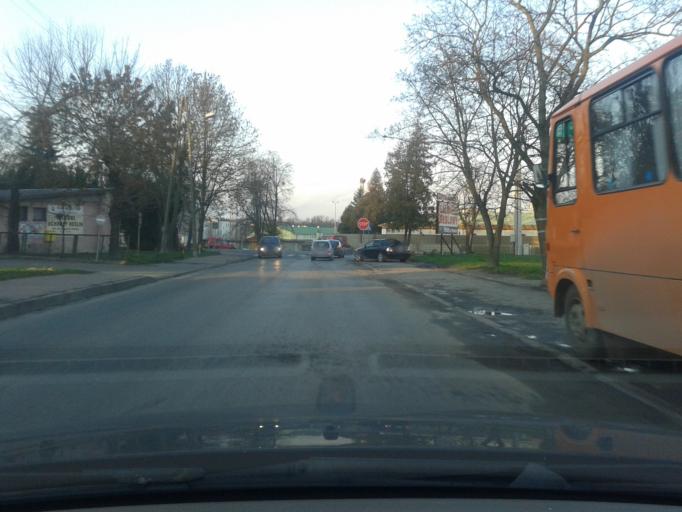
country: PL
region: Lublin Voivodeship
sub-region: Powiat opolski
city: Opole Lubelskie
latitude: 51.1459
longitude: 21.9767
